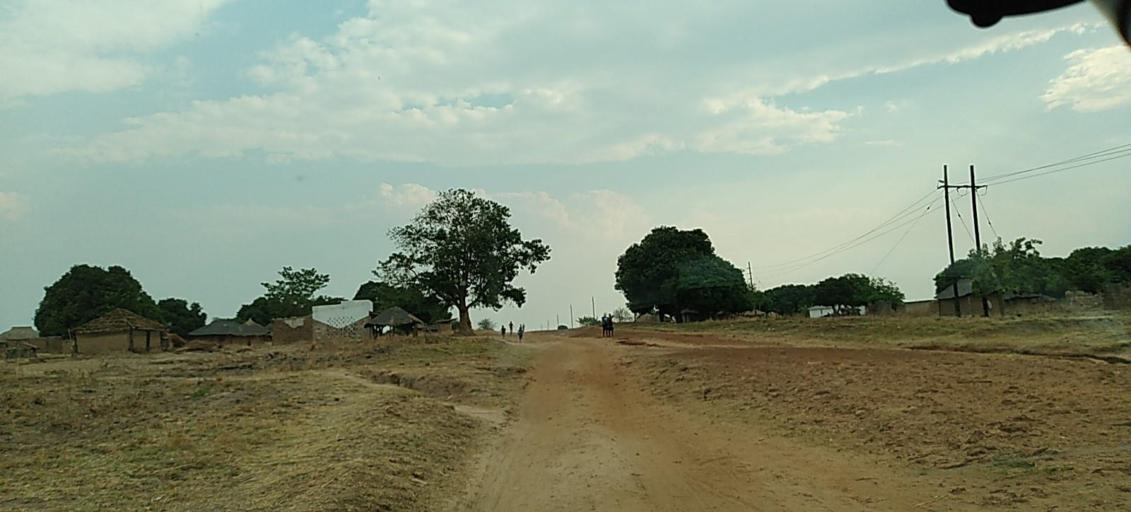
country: ZM
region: North-Western
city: Kabompo
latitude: -13.8669
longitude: 23.6697
